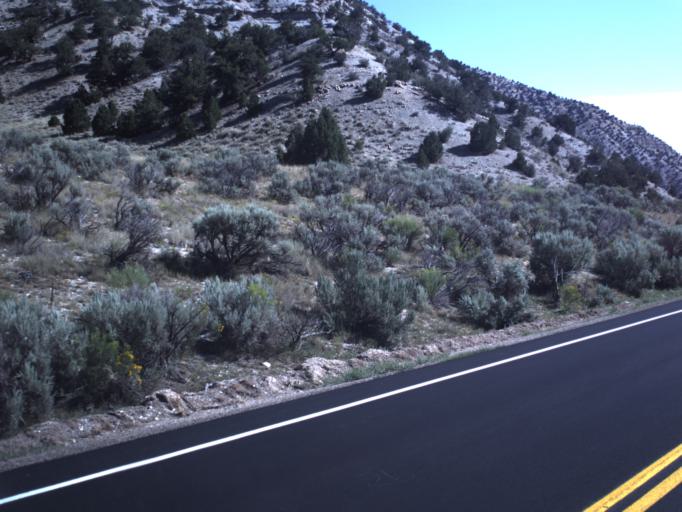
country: US
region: Utah
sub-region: Duchesne County
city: Duchesne
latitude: 39.9629
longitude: -110.6381
